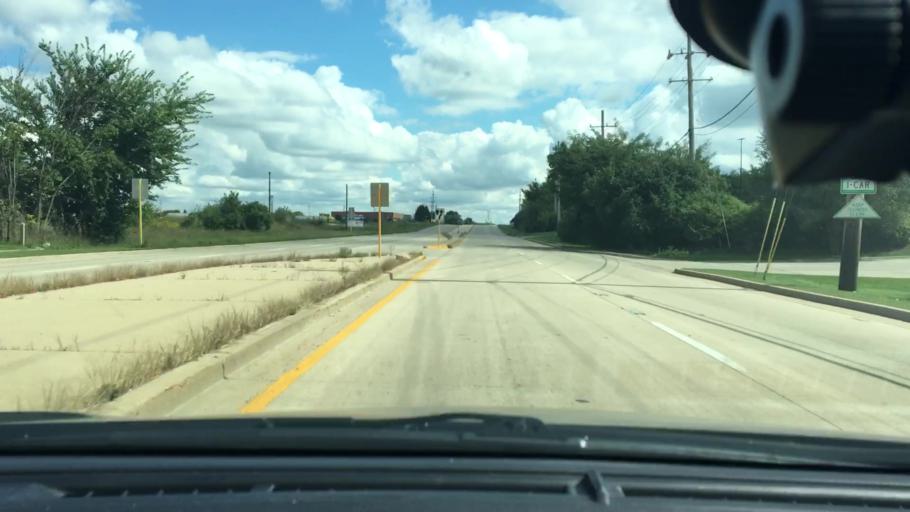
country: US
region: Illinois
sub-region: Kane County
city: East Dundee
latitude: 42.0925
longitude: -88.2558
